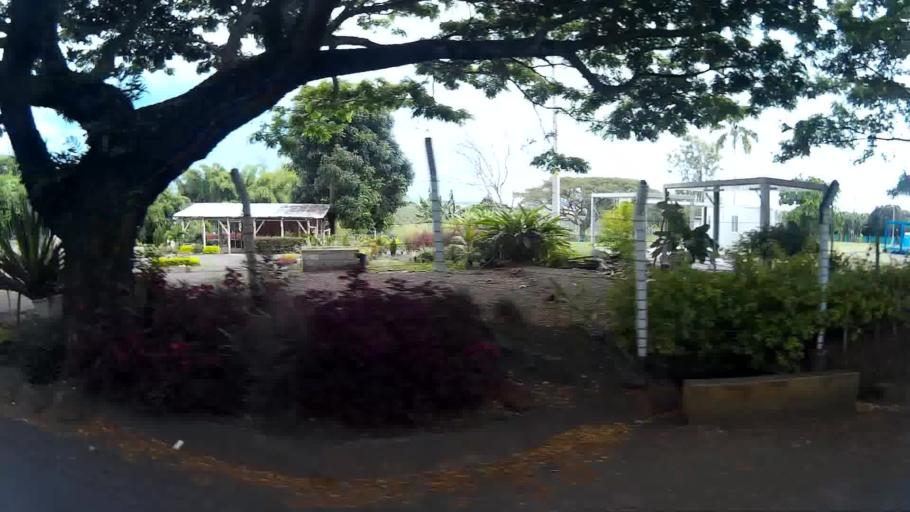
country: CO
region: Risaralda
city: Pereira
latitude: 4.8138
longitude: -75.8023
